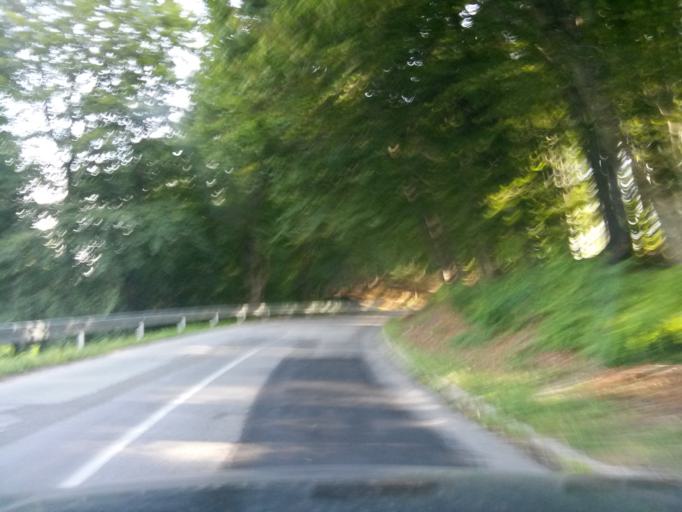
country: HR
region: Grad Zagreb
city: Strmec
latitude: 45.6372
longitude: 15.8688
